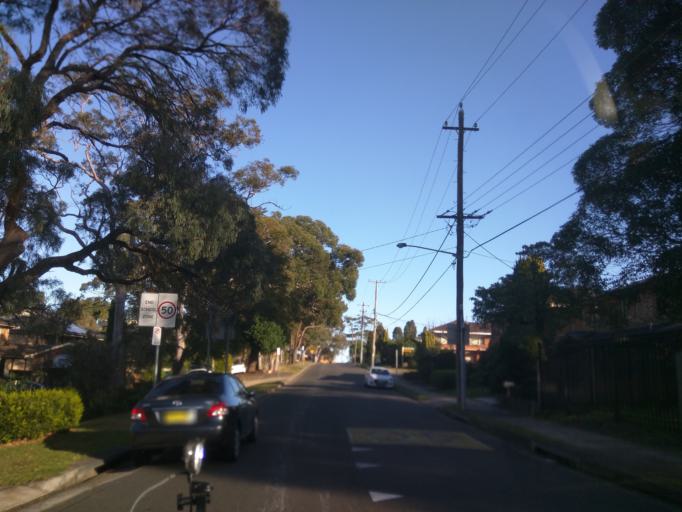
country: AU
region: New South Wales
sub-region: Hurstville
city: Lugarno
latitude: -33.9859
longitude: 151.0437
